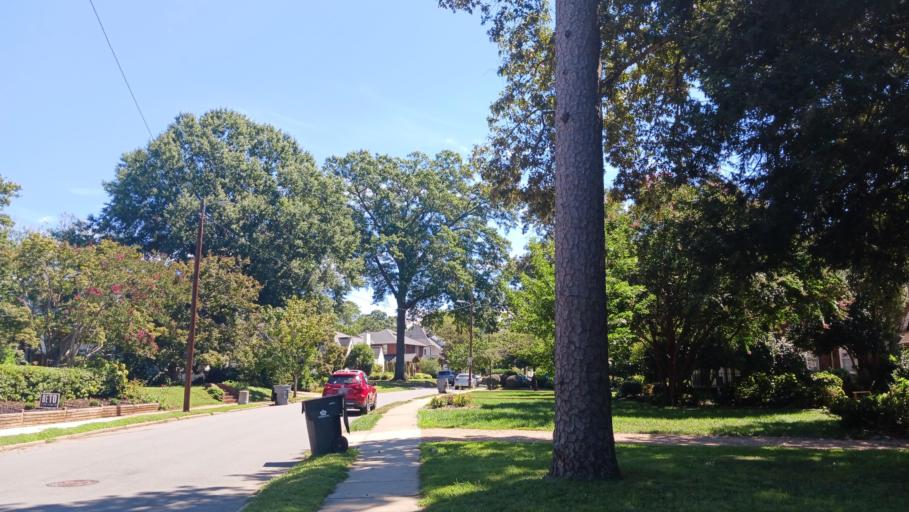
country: US
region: North Carolina
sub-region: Mecklenburg County
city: Charlotte
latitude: 35.2114
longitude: -80.8192
